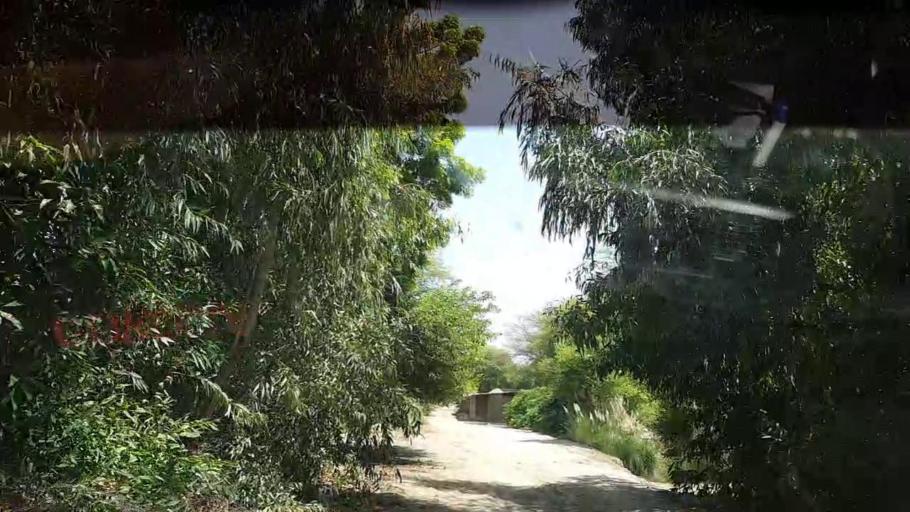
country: PK
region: Sindh
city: Ghauspur
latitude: 28.1648
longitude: 69.1312
